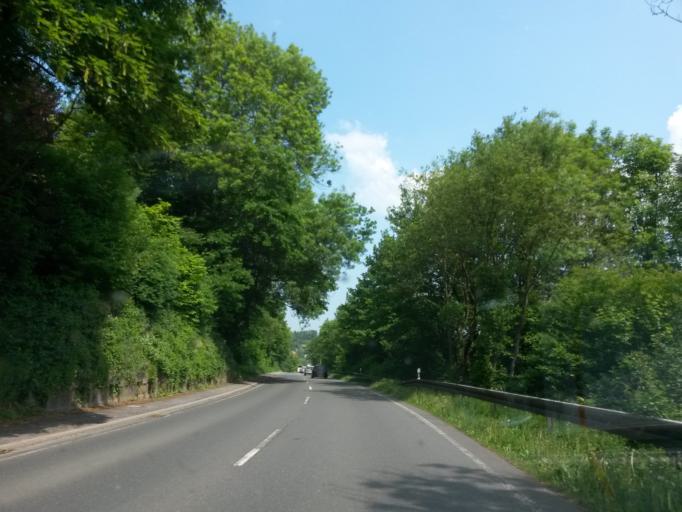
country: DE
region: North Rhine-Westphalia
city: Balve
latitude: 51.3238
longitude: 7.8677
